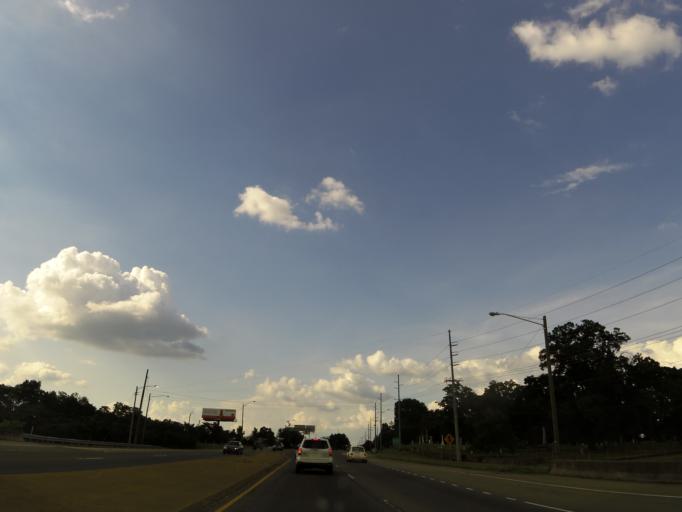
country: US
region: Tennessee
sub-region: Davidson County
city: Goodlettsville
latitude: 36.2352
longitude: -86.7247
